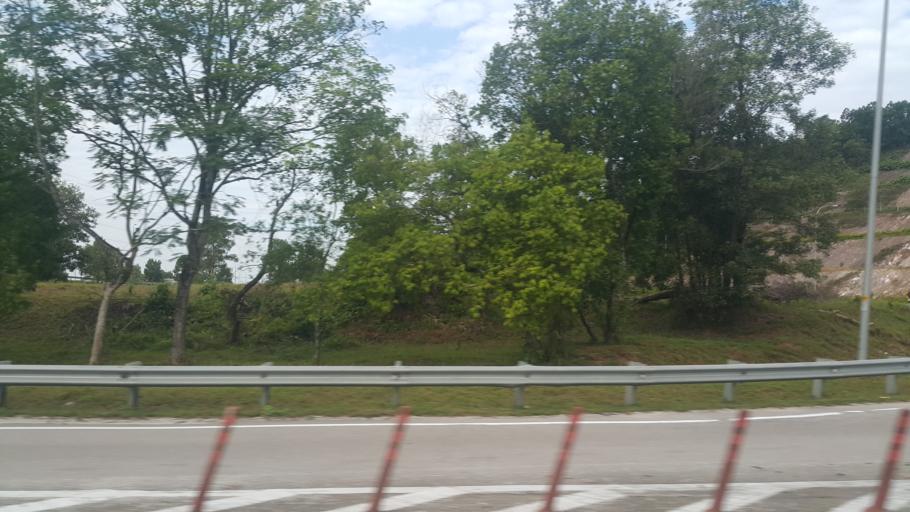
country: MY
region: Johor
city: Skudai
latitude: 1.4534
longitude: 103.6137
